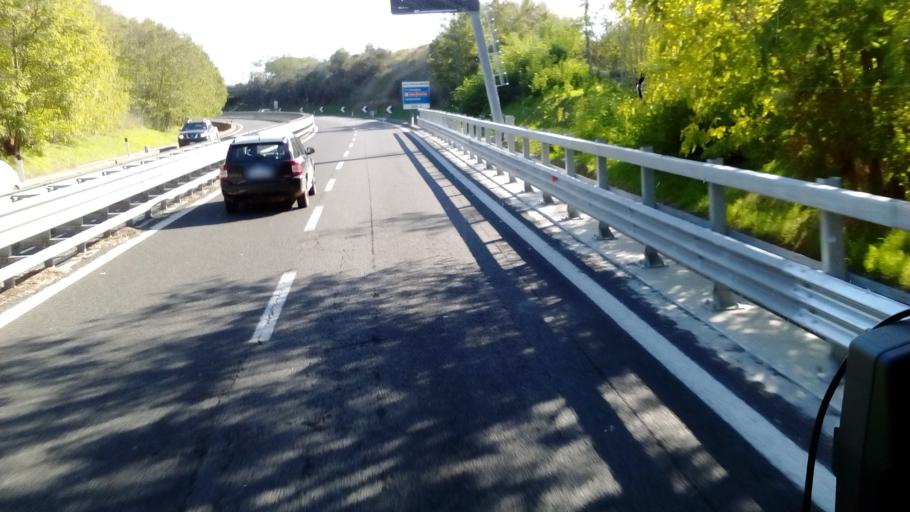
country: IT
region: Latium
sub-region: Provincia di Viterbo
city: Montalto di Castro
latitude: 42.3126
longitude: 11.6537
